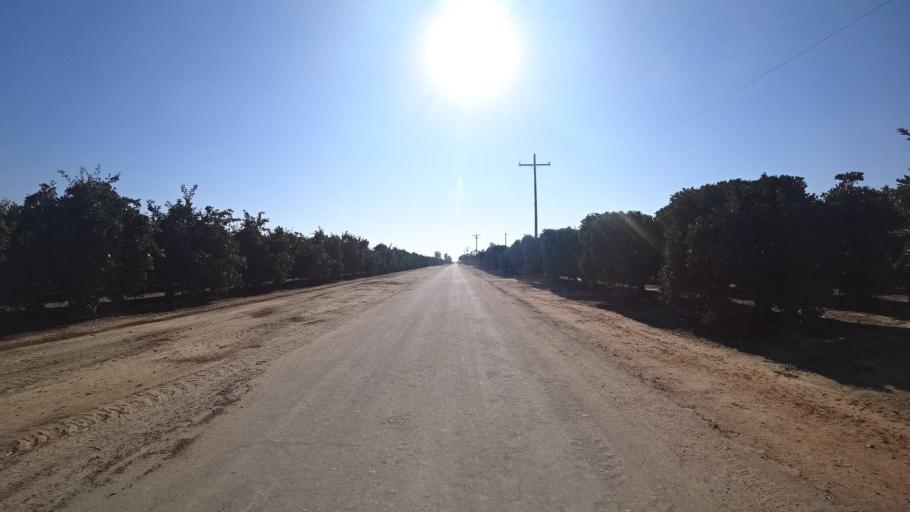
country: US
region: California
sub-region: Tulare County
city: Richgrove
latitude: 35.7301
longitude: -119.1429
